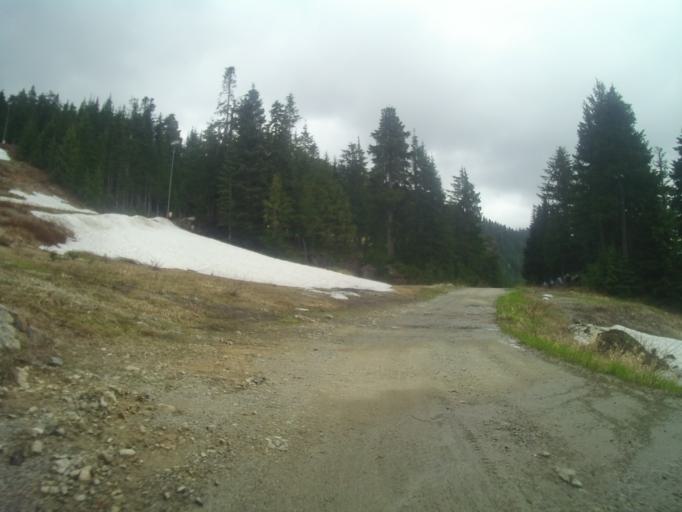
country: CA
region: British Columbia
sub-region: Fraser Valley Regional District
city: North Vancouver
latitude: 49.3786
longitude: -123.0740
